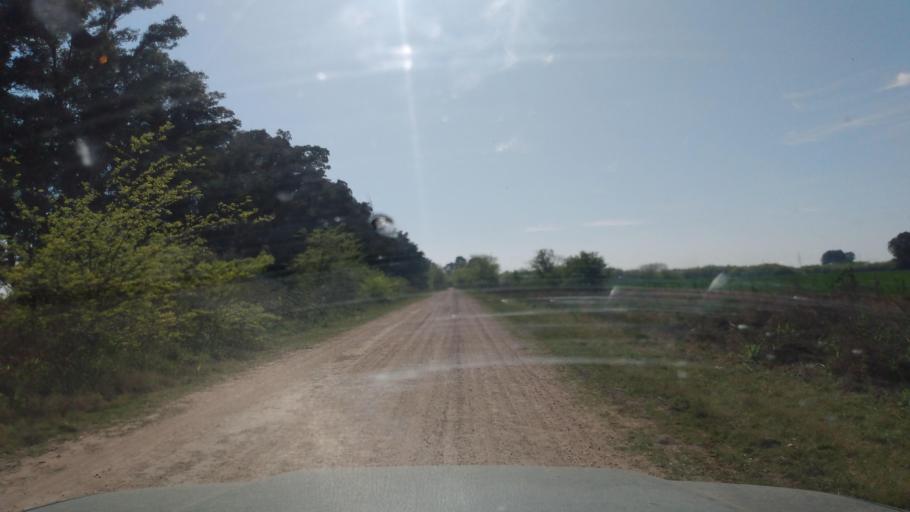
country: AR
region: Buenos Aires
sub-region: Partido de Lujan
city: Lujan
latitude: -34.6293
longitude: -59.1021
